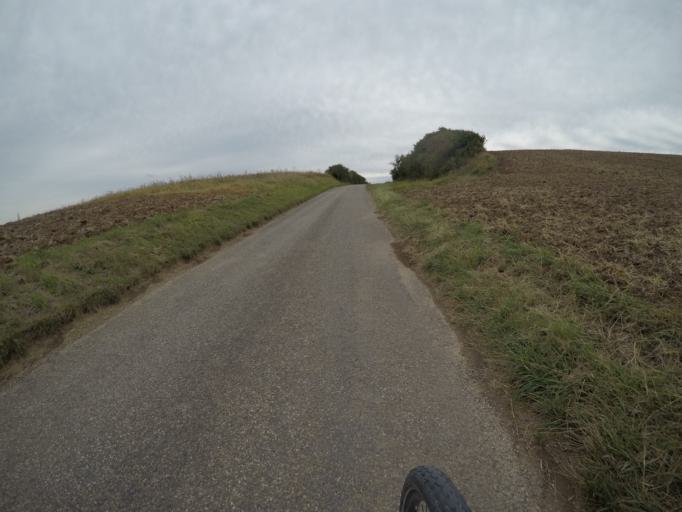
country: DE
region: Baden-Wuerttemberg
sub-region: Karlsruhe Region
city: Muhlacker
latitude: 48.9852
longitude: 8.8500
